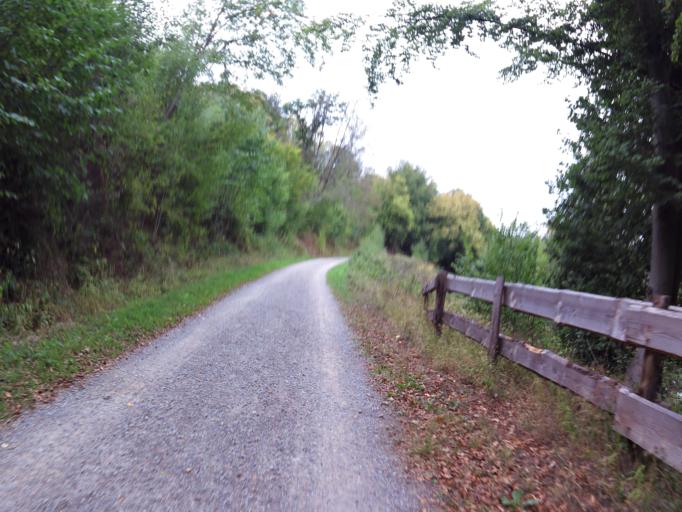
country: DE
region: North Rhine-Westphalia
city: Heimbach
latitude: 50.6356
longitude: 6.4280
